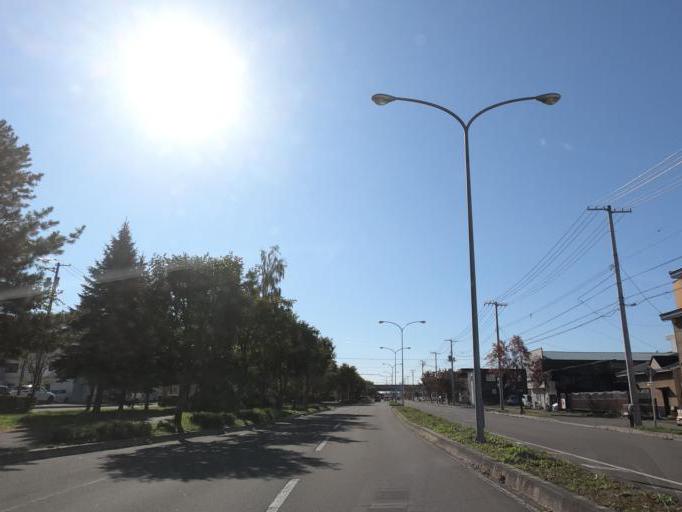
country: JP
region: Hokkaido
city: Obihiro
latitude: 42.9169
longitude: 143.2126
